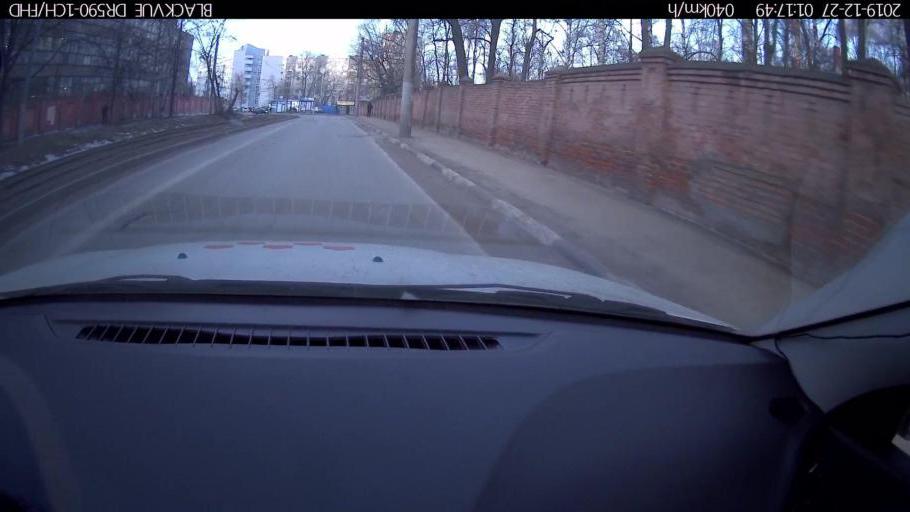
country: RU
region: Nizjnij Novgorod
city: Nizhniy Novgorod
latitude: 56.3004
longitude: 43.9918
